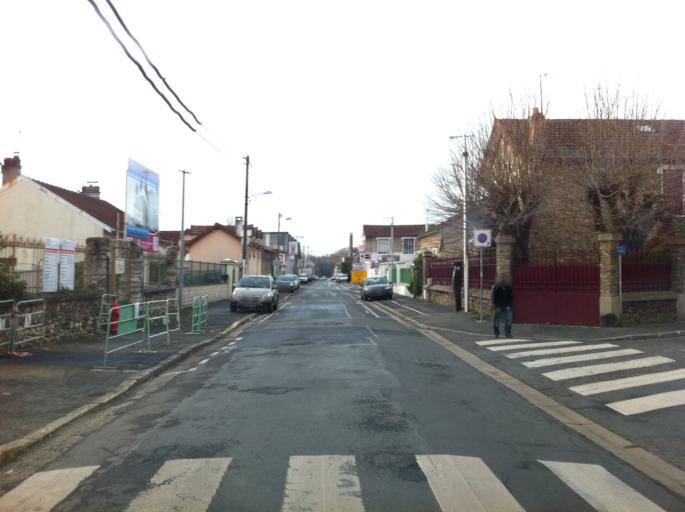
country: FR
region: Ile-de-France
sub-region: Departement de Seine-et-Marne
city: Dammarie-les-Lys
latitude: 48.5308
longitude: 2.6490
